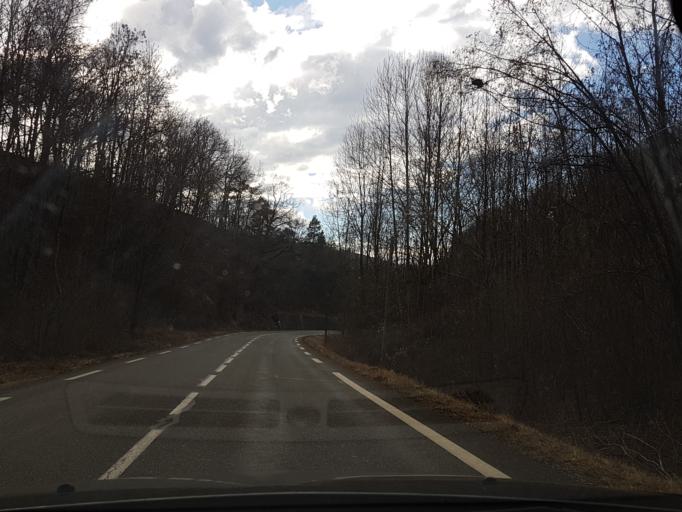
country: FR
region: Provence-Alpes-Cote d'Azur
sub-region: Departement des Hautes-Alpes
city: Tallard
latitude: 44.4869
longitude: 6.0796
